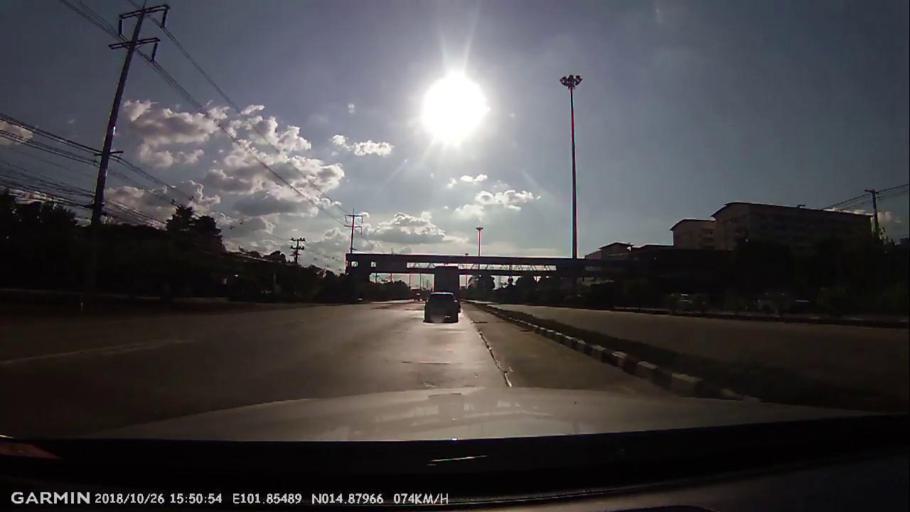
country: TH
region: Nakhon Ratchasima
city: Sung Noen
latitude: 14.8796
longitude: 101.8547
